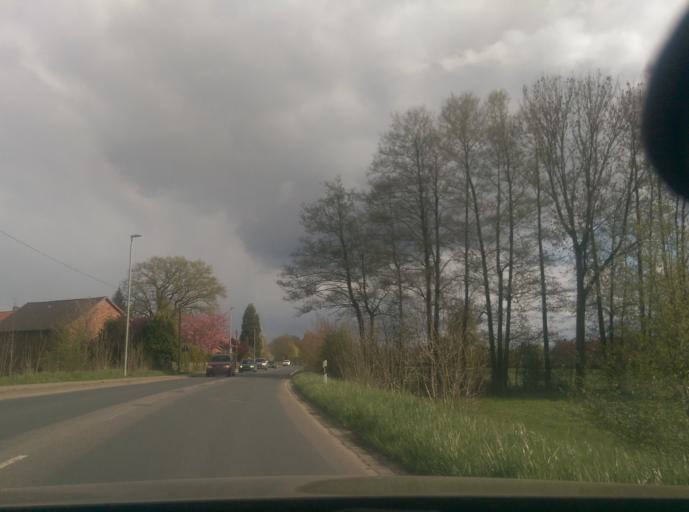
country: DE
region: Lower Saxony
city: Lindwedel
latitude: 52.5681
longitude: 9.6183
